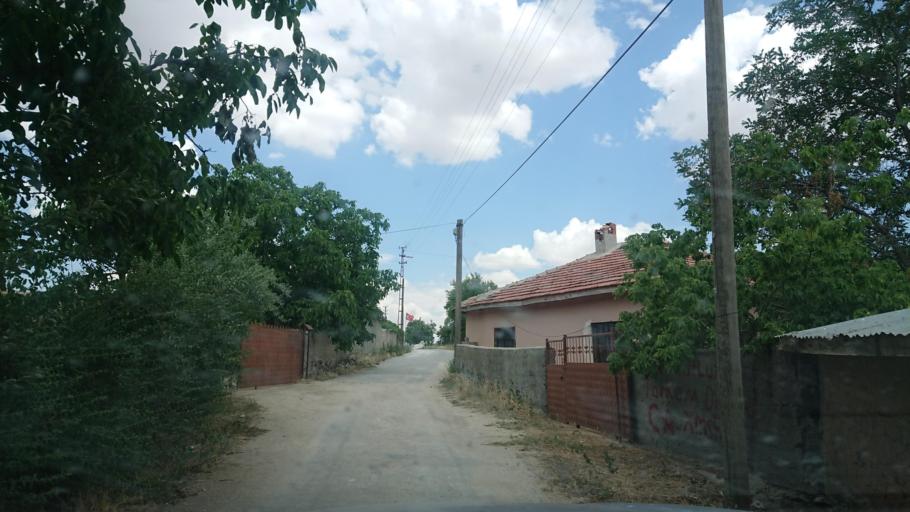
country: TR
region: Aksaray
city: Agacoren
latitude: 38.8880
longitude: 33.8808
